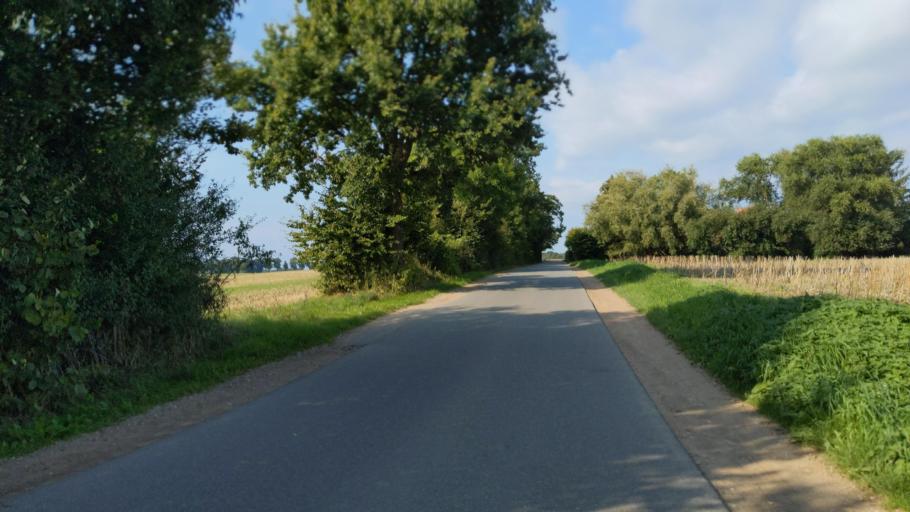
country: DE
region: Mecklenburg-Vorpommern
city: Kalkhorst
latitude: 53.9675
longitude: 11.0089
